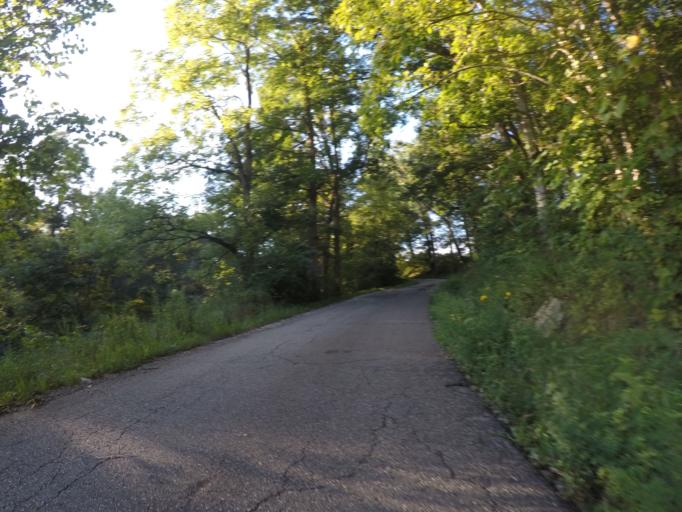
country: US
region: Ohio
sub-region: Lawrence County
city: Coal Grove
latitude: 38.5829
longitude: -82.5487
